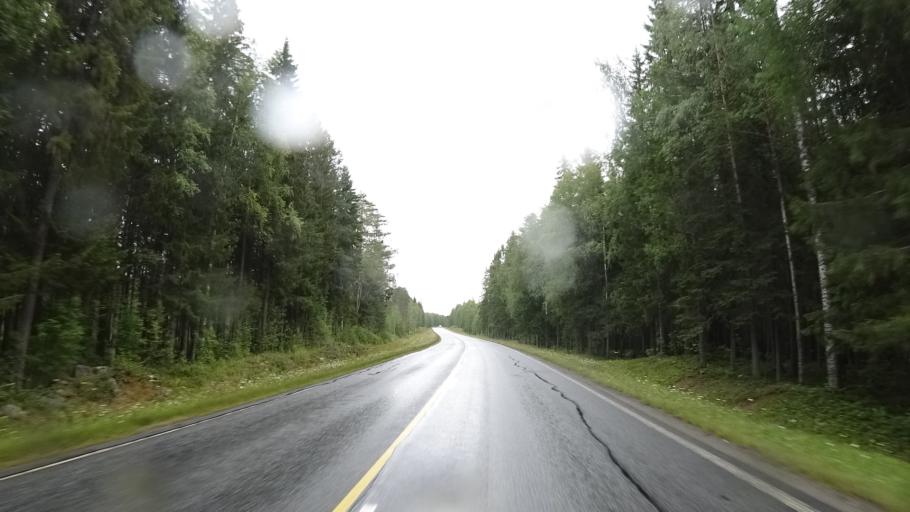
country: FI
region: North Karelia
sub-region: Keski-Karjala
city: Kesaelahti
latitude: 62.1073
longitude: 29.7904
